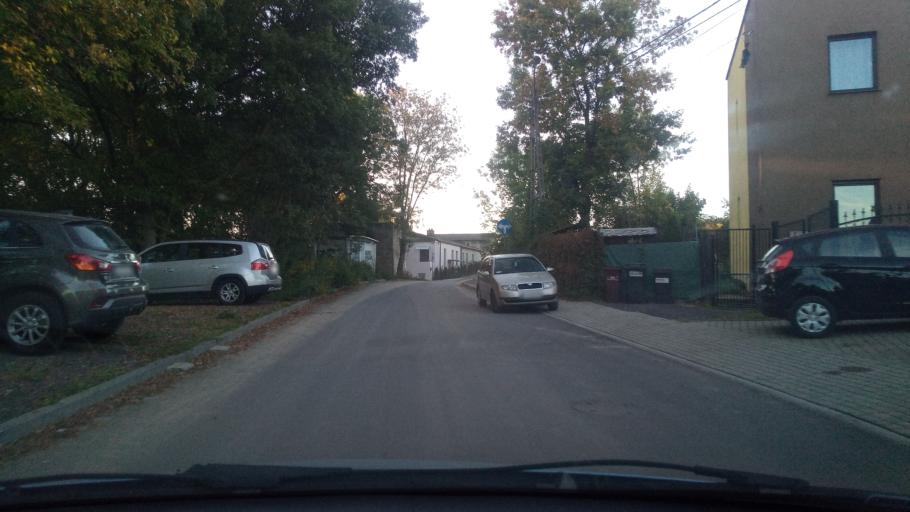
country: PL
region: Silesian Voivodeship
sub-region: Sosnowiec
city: Sosnowiec
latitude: 50.2869
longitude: 19.0753
